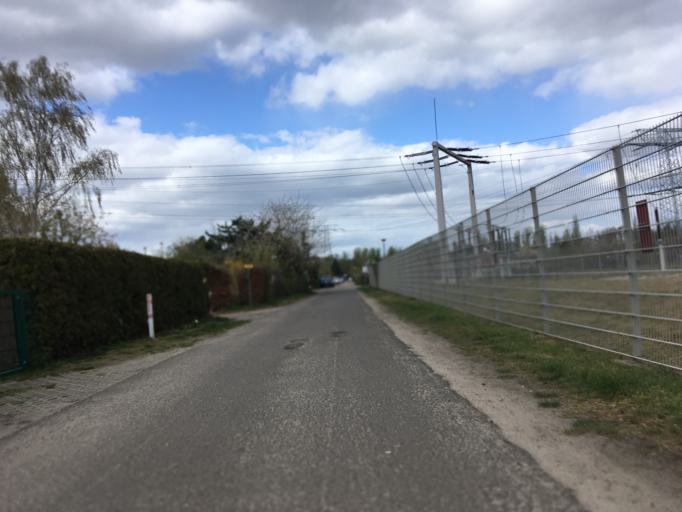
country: DE
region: Berlin
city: Baumschulenweg
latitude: 52.4738
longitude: 13.5043
